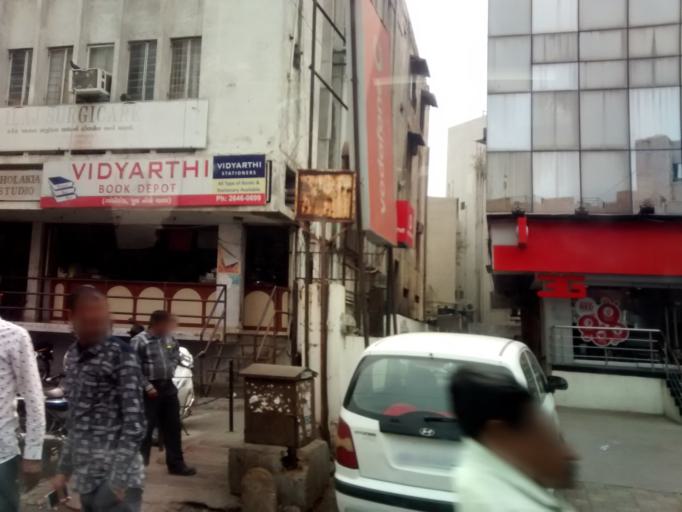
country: IN
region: Gujarat
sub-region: Ahmadabad
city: Ahmedabad
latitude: 23.0398
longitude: 72.5631
